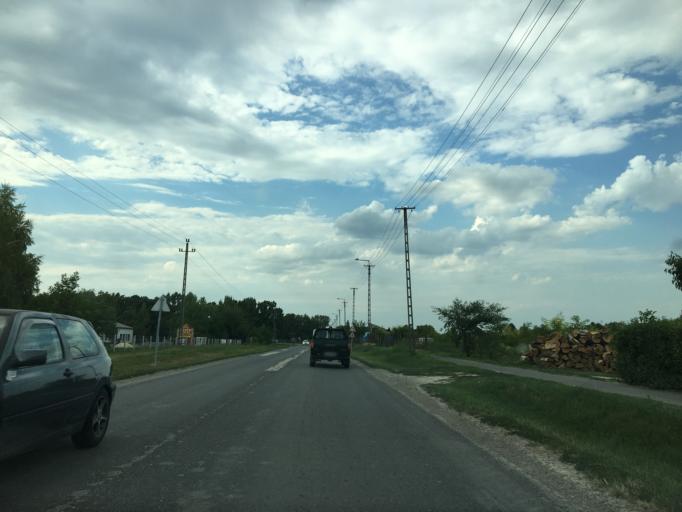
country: HU
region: Bacs-Kiskun
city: Dusnok
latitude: 46.3806
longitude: 18.9596
